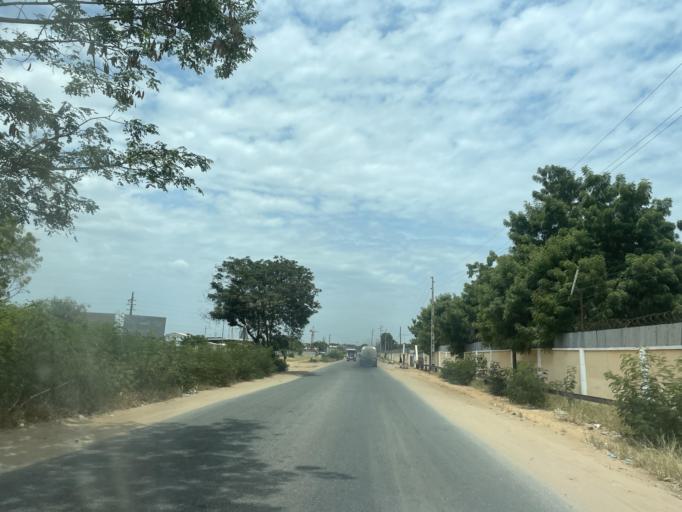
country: AO
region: Luanda
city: Luanda
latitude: -8.9354
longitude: 13.3910
